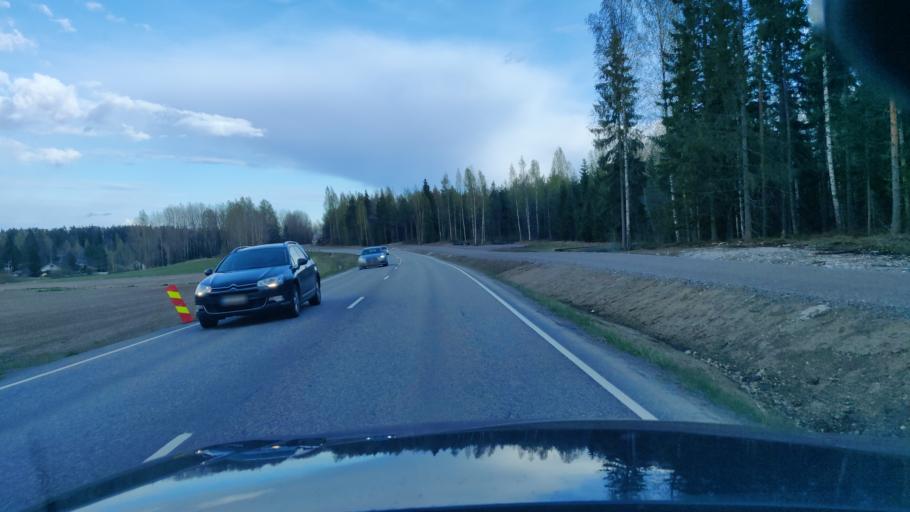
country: FI
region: Uusimaa
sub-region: Helsinki
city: Jaervenpaeae
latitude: 60.4803
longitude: 25.0592
